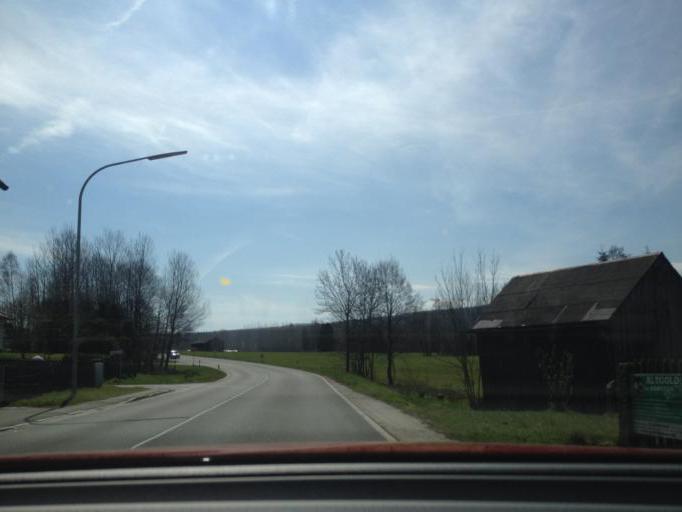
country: DE
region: Bavaria
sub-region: Upper Franconia
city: Oberhaid
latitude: 50.0950
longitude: 11.7928
